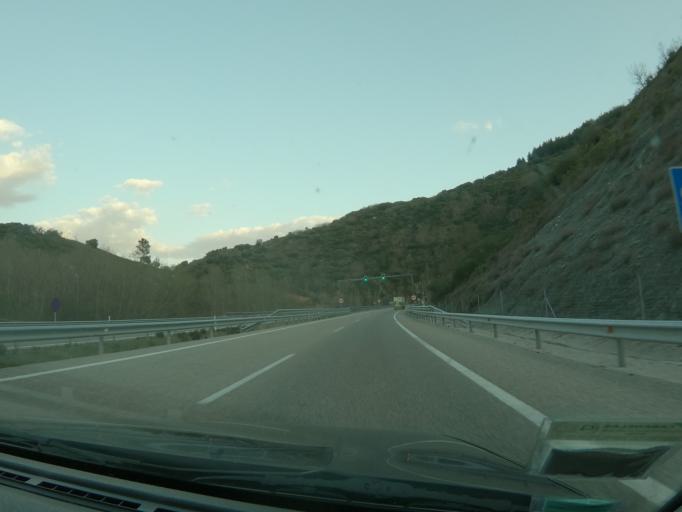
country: ES
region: Castille and Leon
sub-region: Provincia de Leon
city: Villafranca del Bierzo
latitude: 42.6135
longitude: -6.8227
